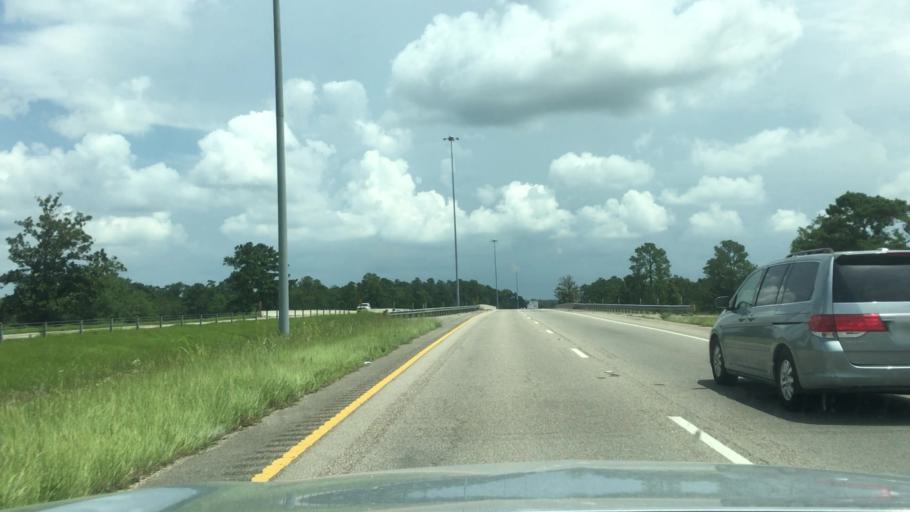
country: US
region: Mississippi
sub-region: Pearl River County
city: Picayune
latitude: 30.5163
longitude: -89.6639
